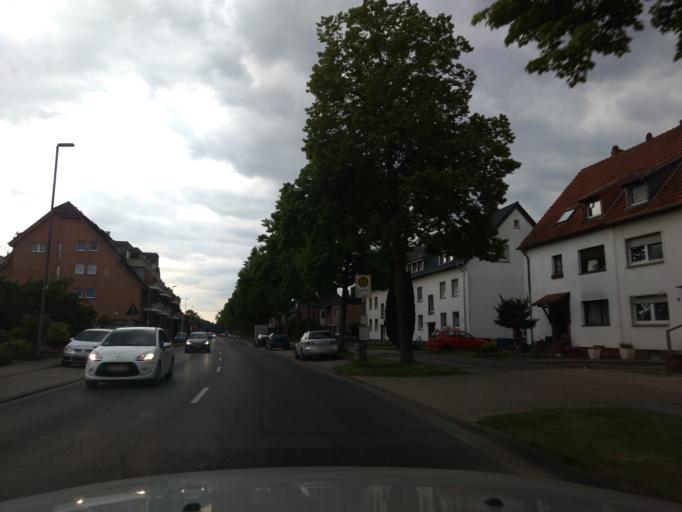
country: DE
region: North Rhine-Westphalia
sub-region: Regierungsbezirk Dusseldorf
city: Willich
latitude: 51.2399
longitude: 6.5341
